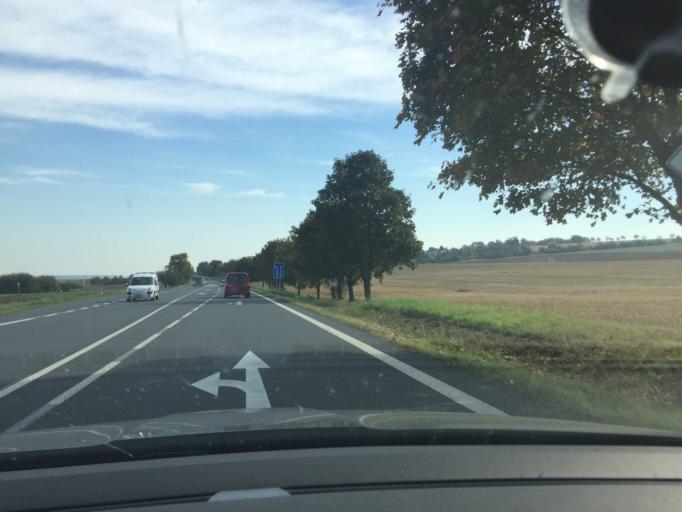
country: CZ
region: Central Bohemia
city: Velim
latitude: 50.0381
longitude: 15.1196
